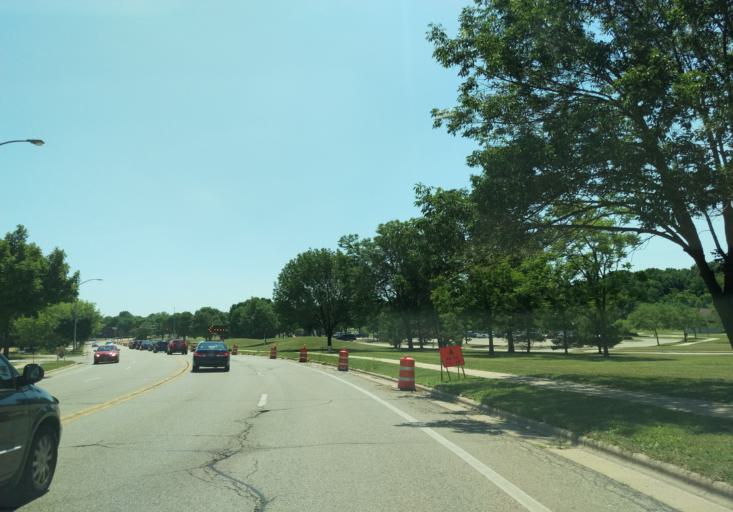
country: US
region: Wisconsin
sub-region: Dane County
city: Verona
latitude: 43.0395
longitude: -89.5043
